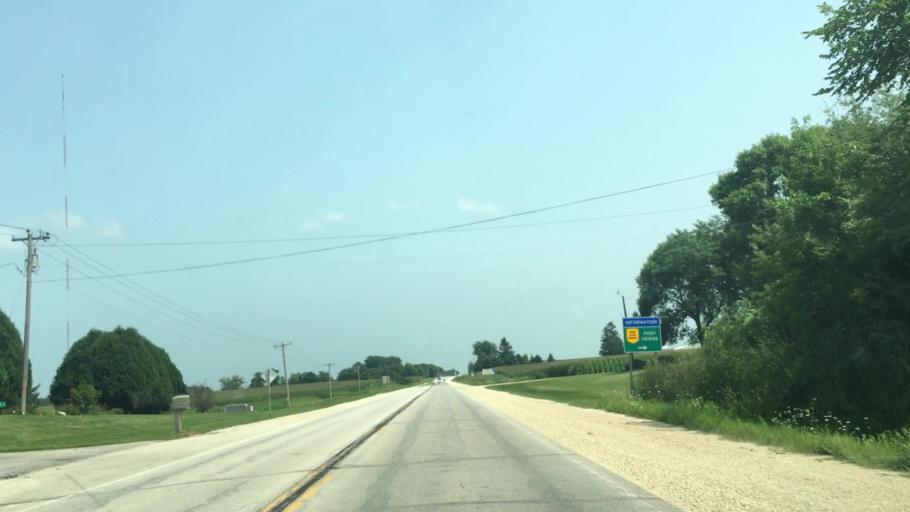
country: US
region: Iowa
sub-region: Fayette County
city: Oelwein
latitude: 42.6792
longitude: -91.8902
